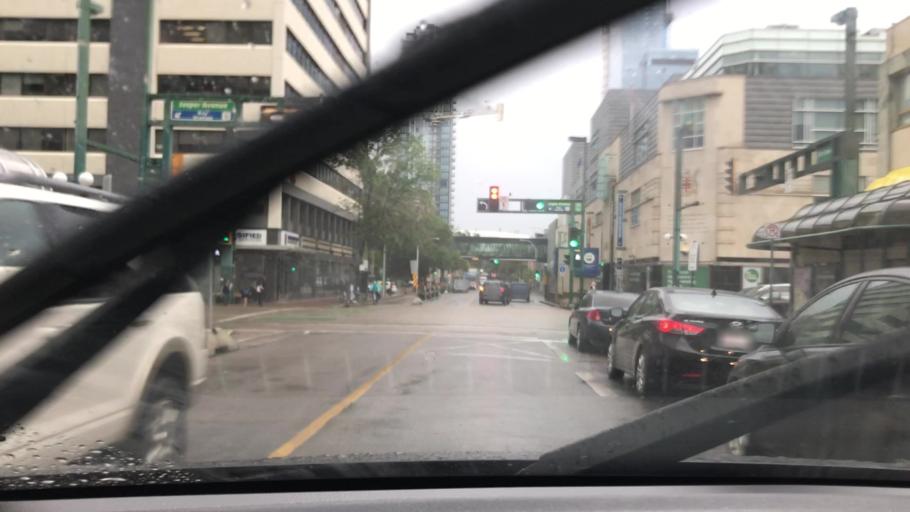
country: CA
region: Alberta
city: Edmonton
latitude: 53.5406
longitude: -113.4974
